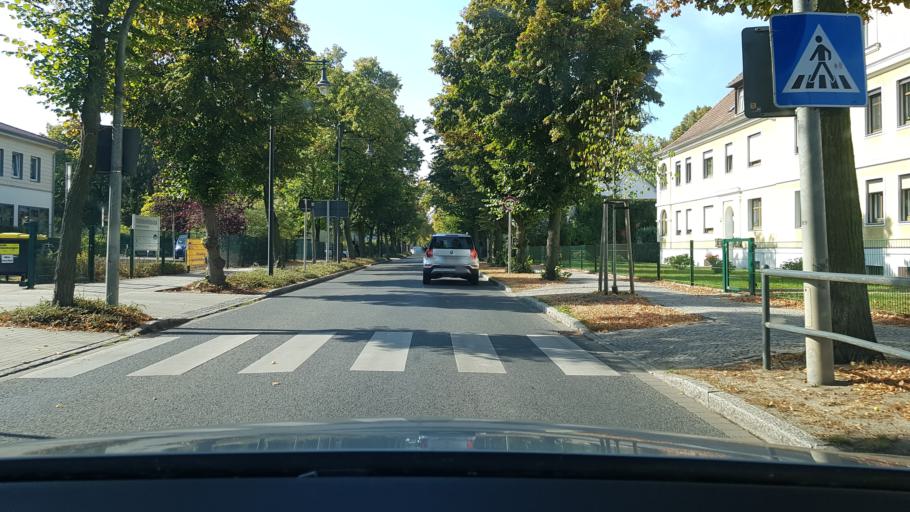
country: DE
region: Brandenburg
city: Beeskow
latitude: 52.1736
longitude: 14.2421
